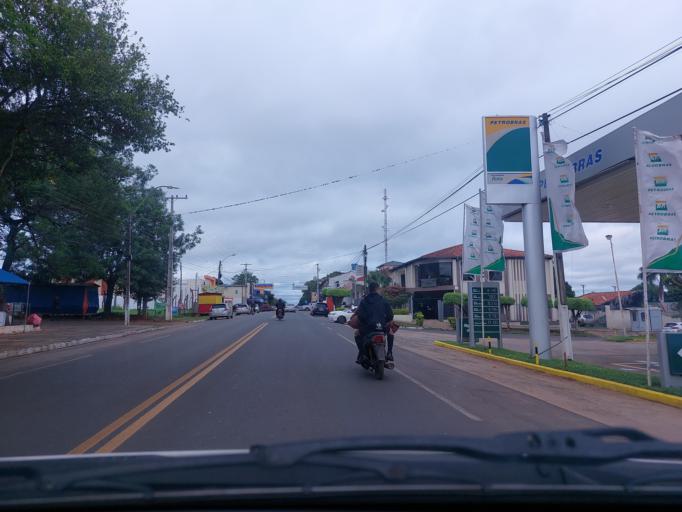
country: PY
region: San Pedro
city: Guayaybi
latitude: -24.6712
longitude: -56.4458
